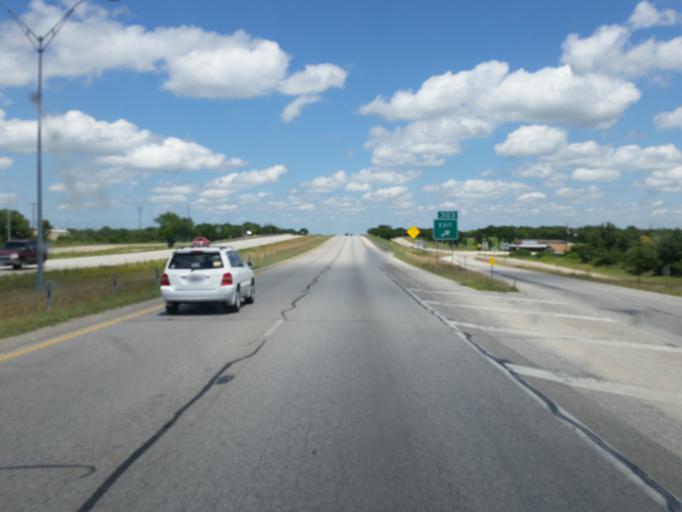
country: US
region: Texas
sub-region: Callahan County
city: Clyde
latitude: 32.4080
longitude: -99.4585
